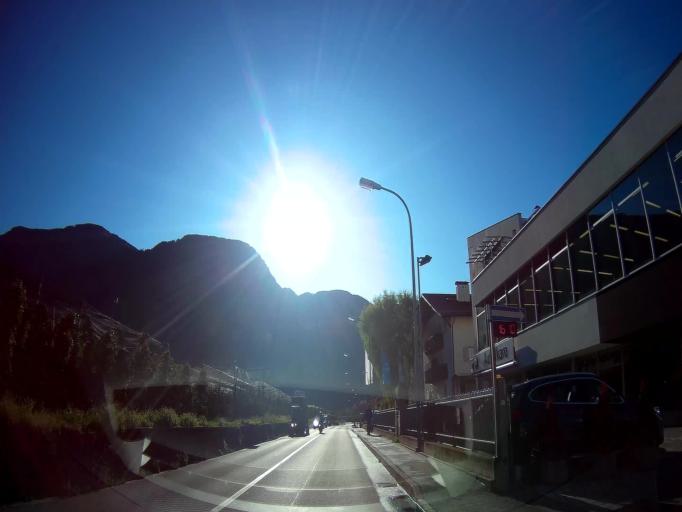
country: IT
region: Trentino-Alto Adige
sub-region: Bolzano
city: Merano
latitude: 46.6556
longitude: 11.1695
